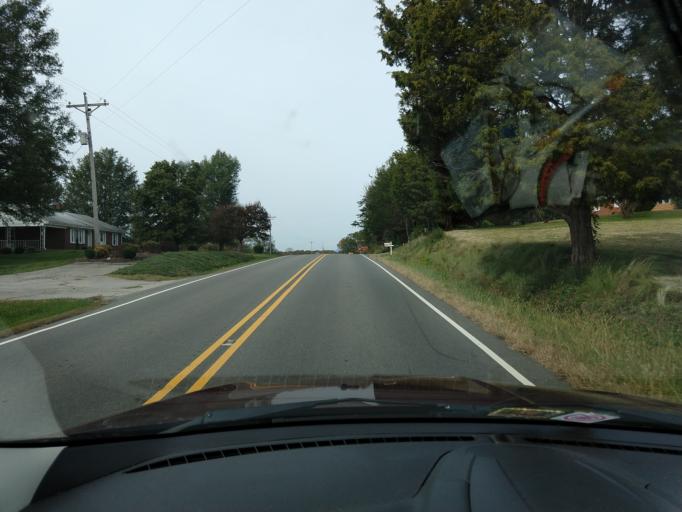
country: US
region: Virginia
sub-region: Franklin County
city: Union Hall
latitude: 36.9677
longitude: -79.5917
